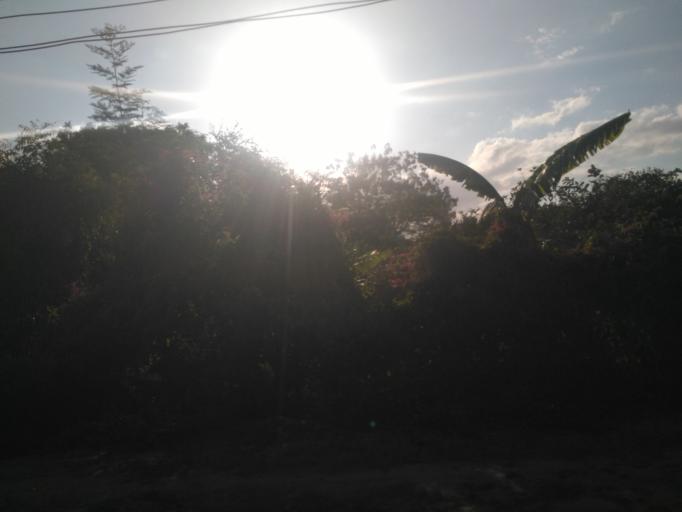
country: TZ
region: Dar es Salaam
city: Magomeni
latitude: -6.7891
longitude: 39.2750
